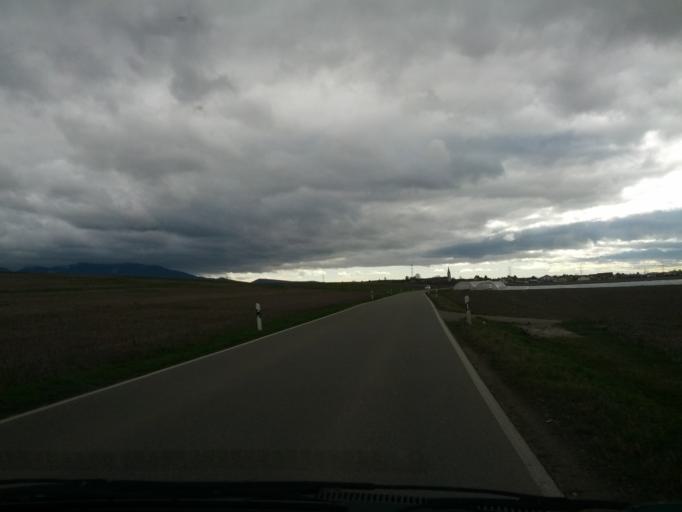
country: DE
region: Baden-Wuerttemberg
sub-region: Freiburg Region
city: Eschbach
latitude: 47.9020
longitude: 7.6597
